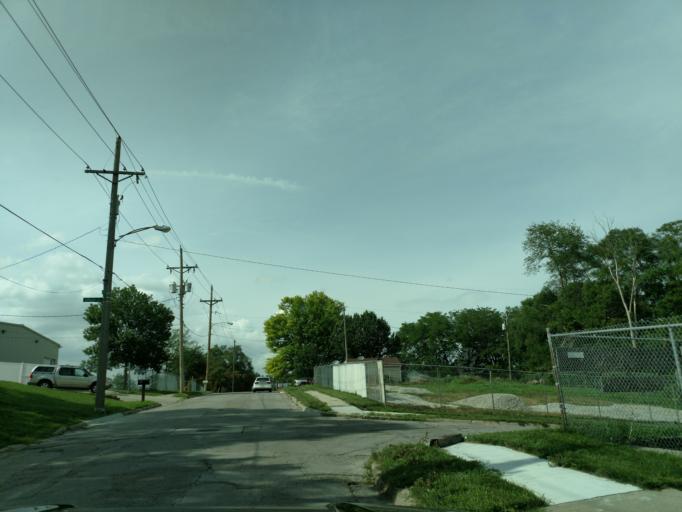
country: US
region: Nebraska
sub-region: Douglas County
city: Omaha
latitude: 41.1953
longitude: -95.9456
